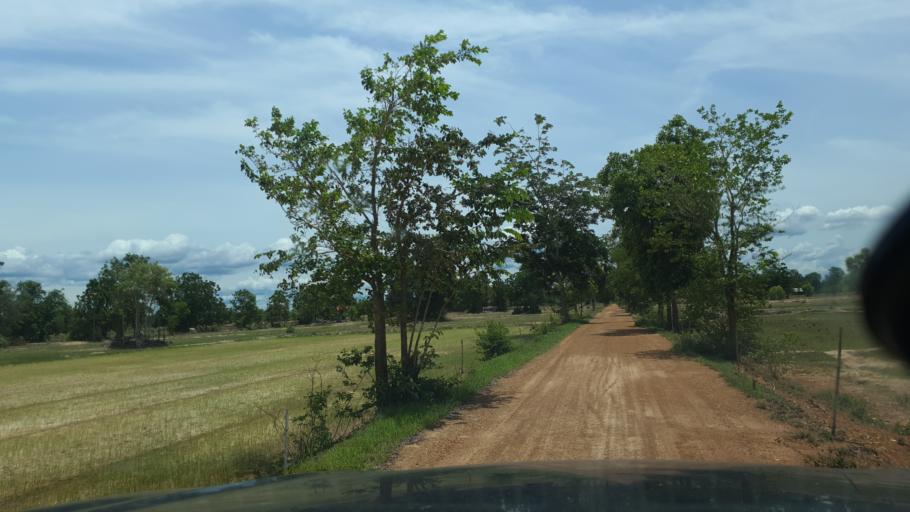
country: TH
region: Sukhothai
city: Ban Na
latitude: 17.1465
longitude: 99.6686
